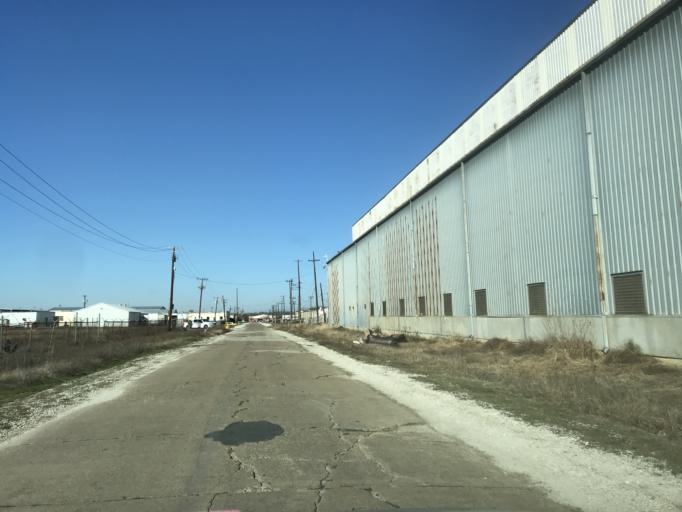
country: US
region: Texas
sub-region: Dallas County
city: Cockrell Hill
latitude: 32.7742
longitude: -96.9018
